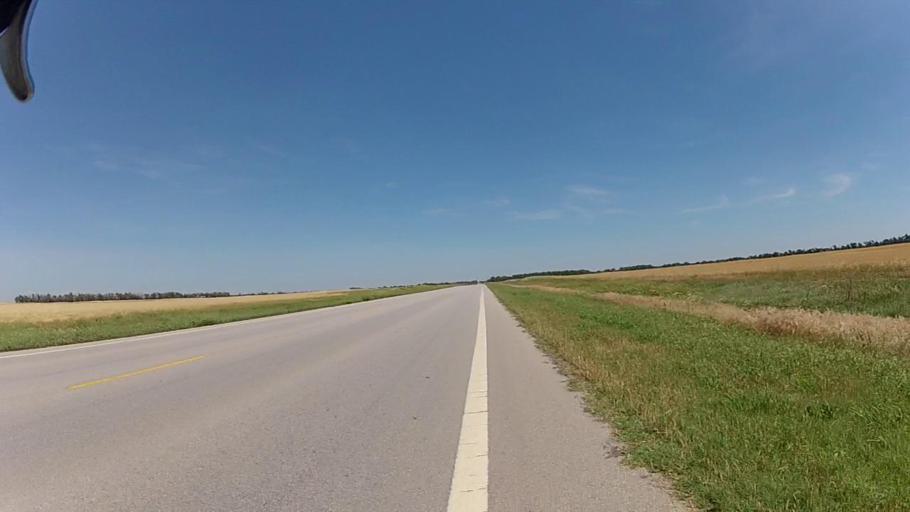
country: US
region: Kansas
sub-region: Harper County
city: Harper
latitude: 37.2387
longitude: -98.1444
